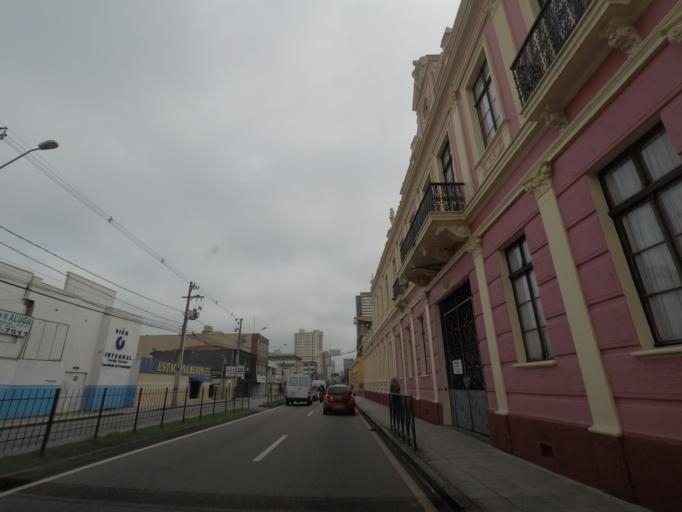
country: BR
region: Parana
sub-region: Curitiba
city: Curitiba
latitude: -25.4409
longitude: -49.2671
